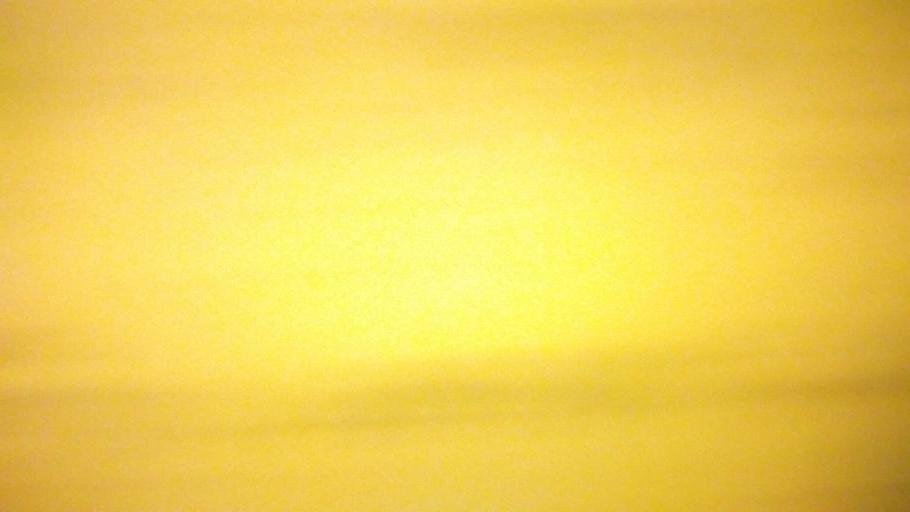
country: TR
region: Duzce
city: Kaynasli
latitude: 40.7577
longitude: 31.4504
